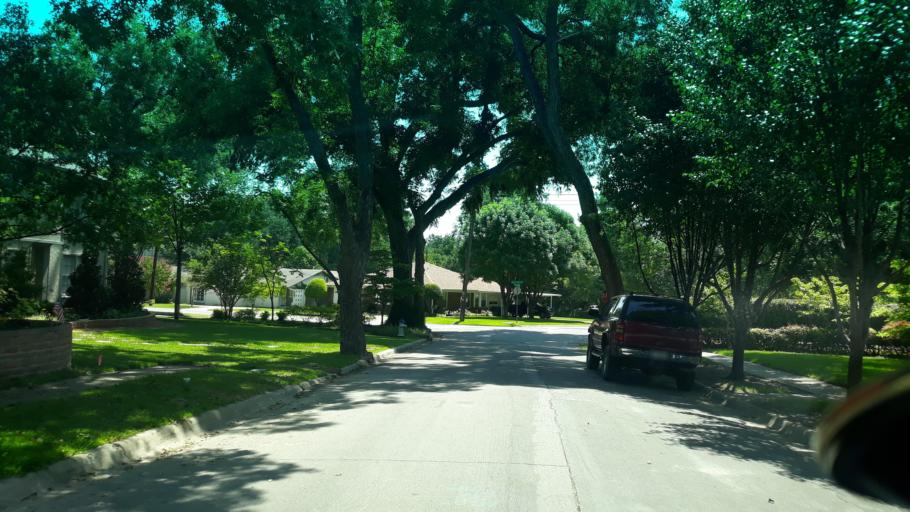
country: US
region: Texas
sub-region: Dallas County
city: Highland Park
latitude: 32.8178
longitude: -96.7350
